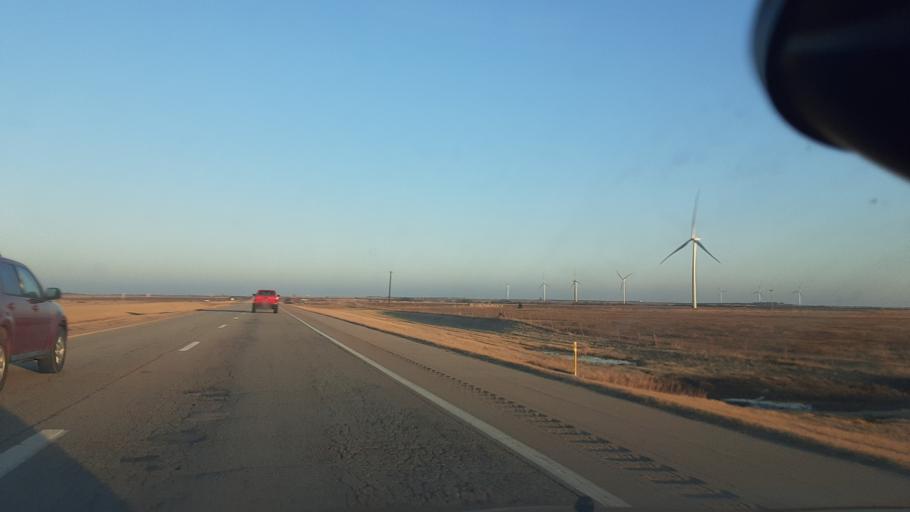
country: US
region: Oklahoma
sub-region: Noble County
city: Perry
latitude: 36.3979
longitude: -97.4110
